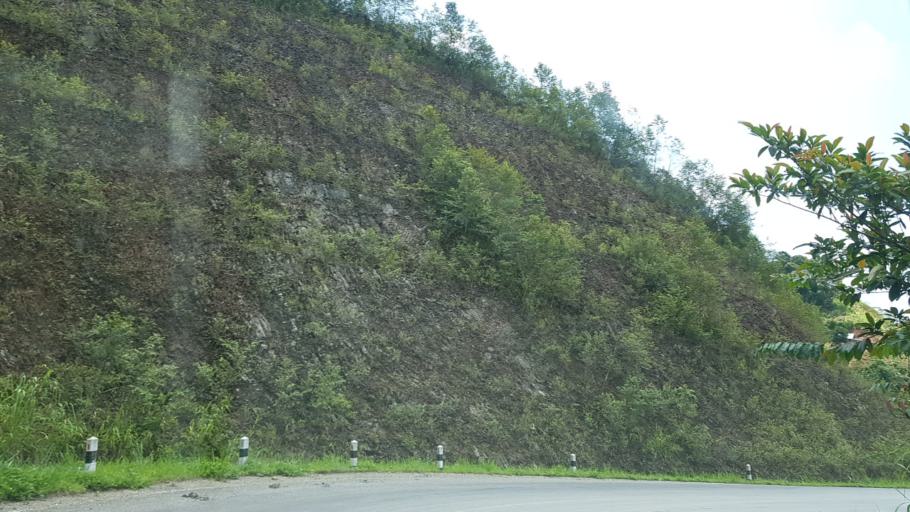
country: LA
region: Vientiane
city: Muang Kasi
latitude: 19.3800
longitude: 102.1557
